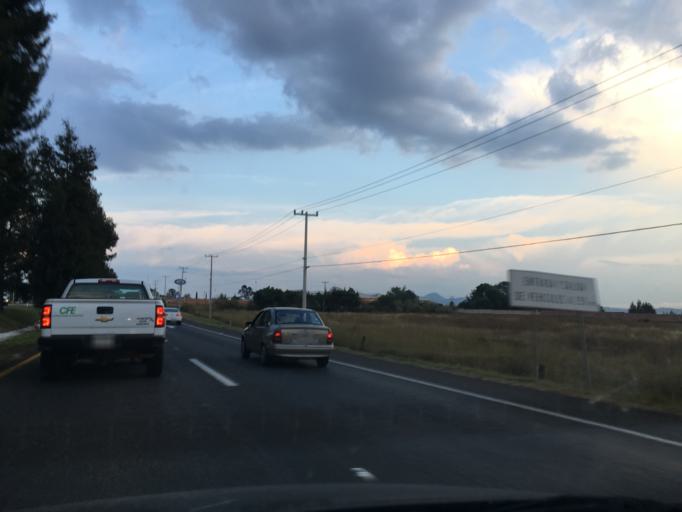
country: MX
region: Michoacan
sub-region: Morelia
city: La Mintzita (Piedra Dura)
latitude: 19.5854
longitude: -101.3048
